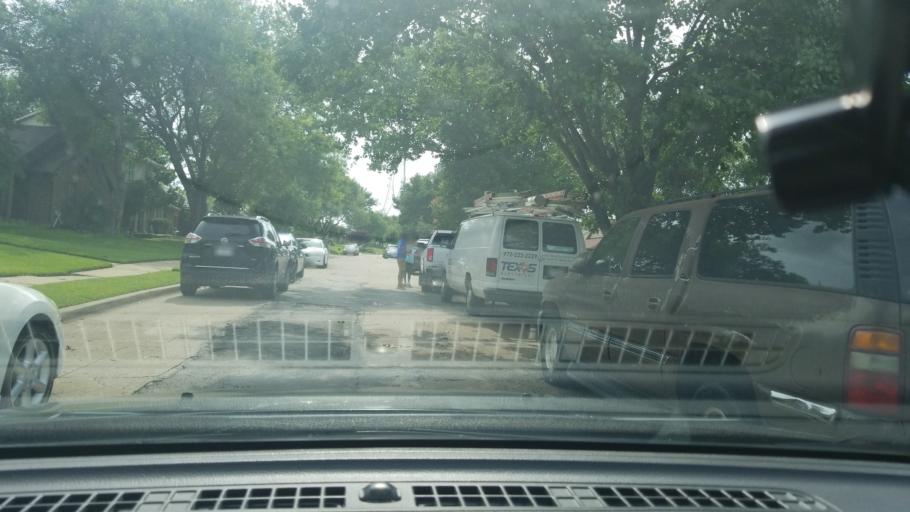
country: US
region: Texas
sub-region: Dallas County
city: Mesquite
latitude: 32.7626
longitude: -96.6283
